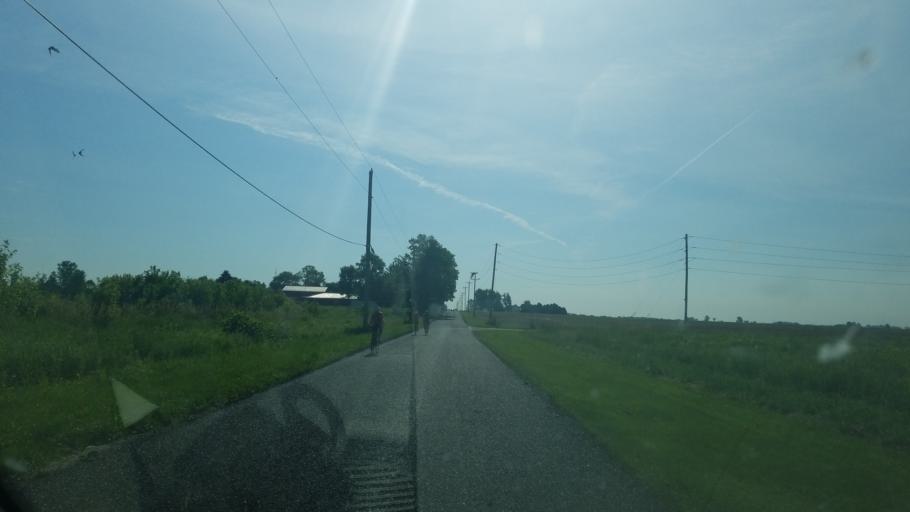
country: US
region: Ohio
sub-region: Hancock County
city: Findlay
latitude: 41.0215
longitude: -83.5558
